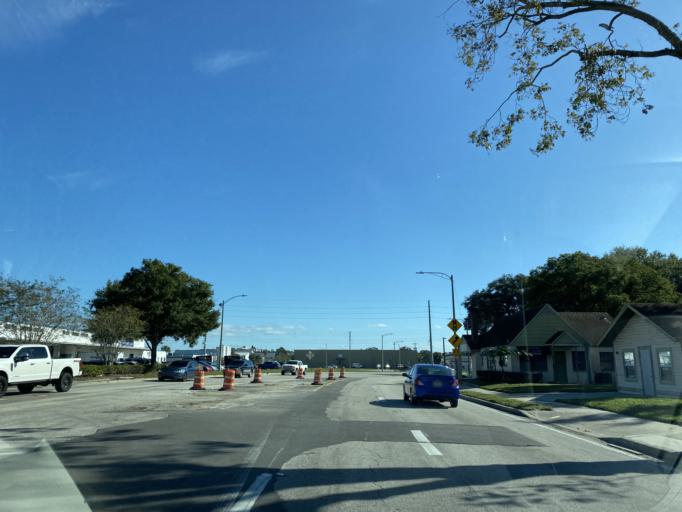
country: US
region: Florida
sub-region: Orange County
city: Holden Heights
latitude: 28.5147
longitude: -81.3866
